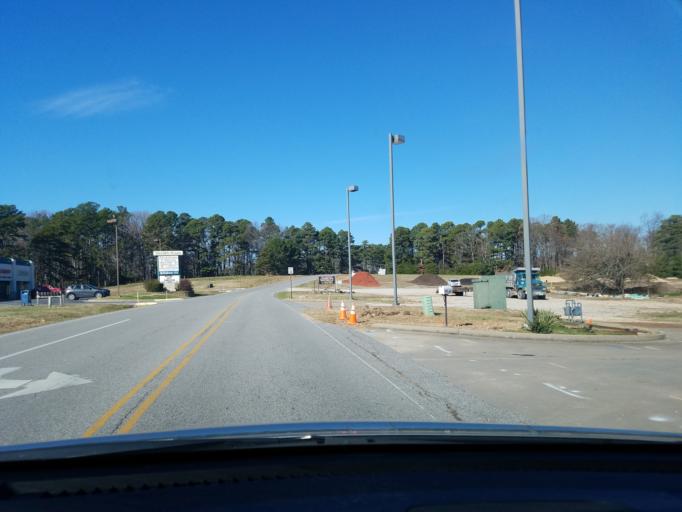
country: US
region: Arkansas
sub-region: Carroll County
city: Eureka Springs
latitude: 36.3925
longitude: -93.7096
